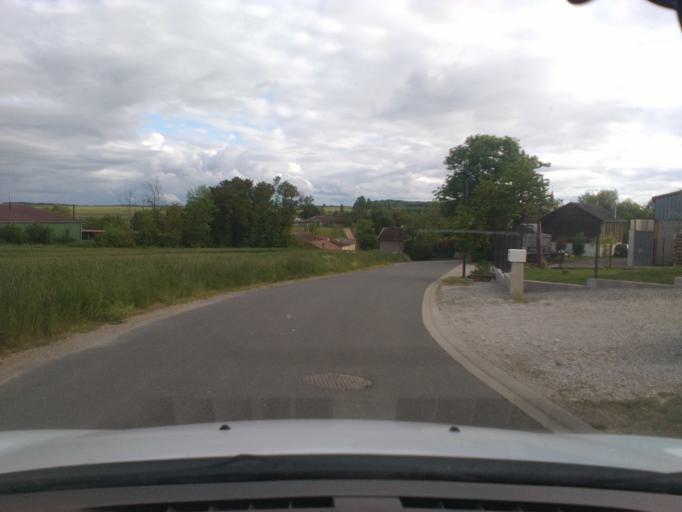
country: FR
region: Lorraine
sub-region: Departement des Vosges
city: Mirecourt
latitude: 48.3381
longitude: 6.1005
